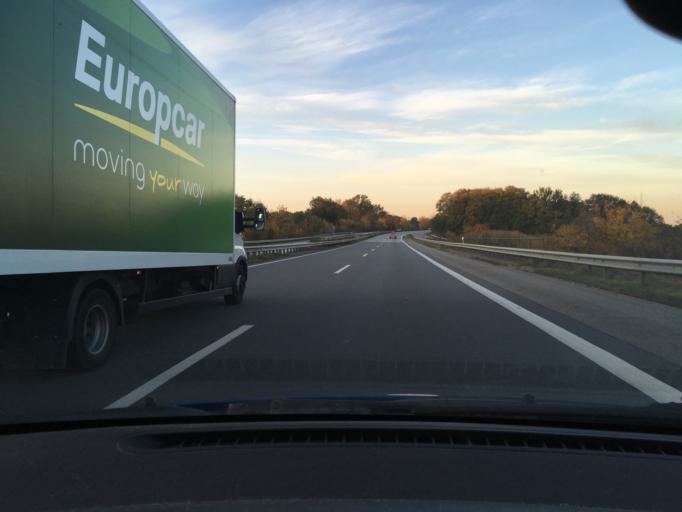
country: DE
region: Schleswig-Holstein
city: Neversdorf
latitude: 53.8570
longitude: 10.3055
